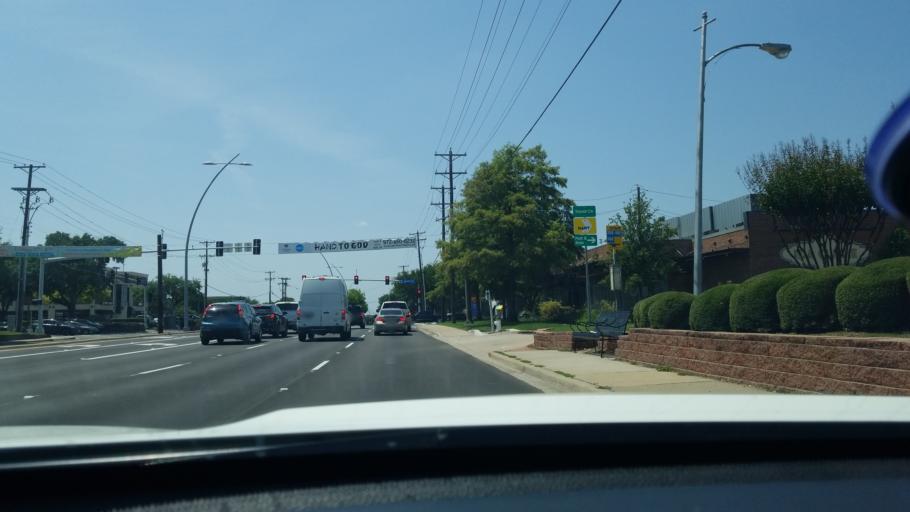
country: US
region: Texas
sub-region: Dallas County
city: Addison
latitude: 32.9542
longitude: -96.8253
